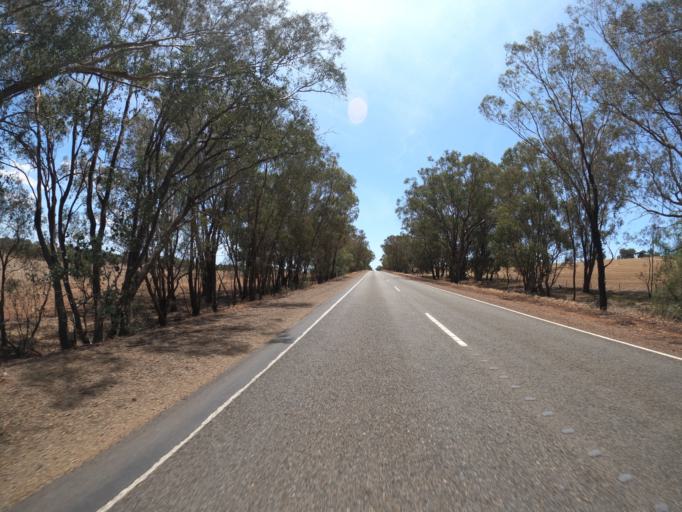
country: AU
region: Victoria
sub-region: Benalla
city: Benalla
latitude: -36.3523
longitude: 145.9635
